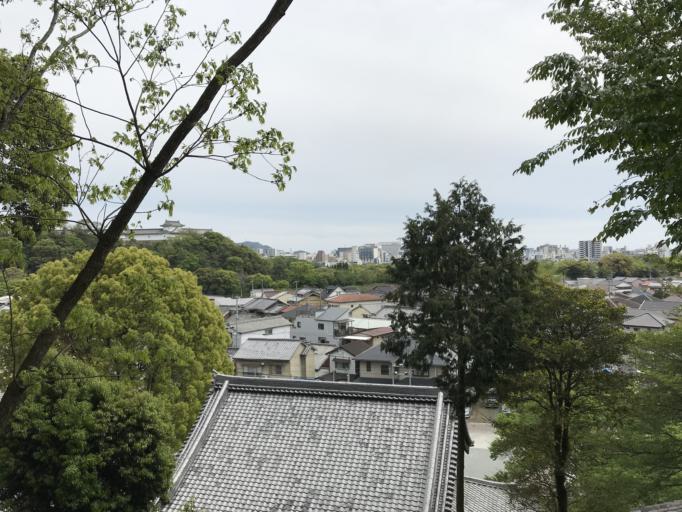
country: JP
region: Hyogo
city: Himeji
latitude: 34.8415
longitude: 134.6893
